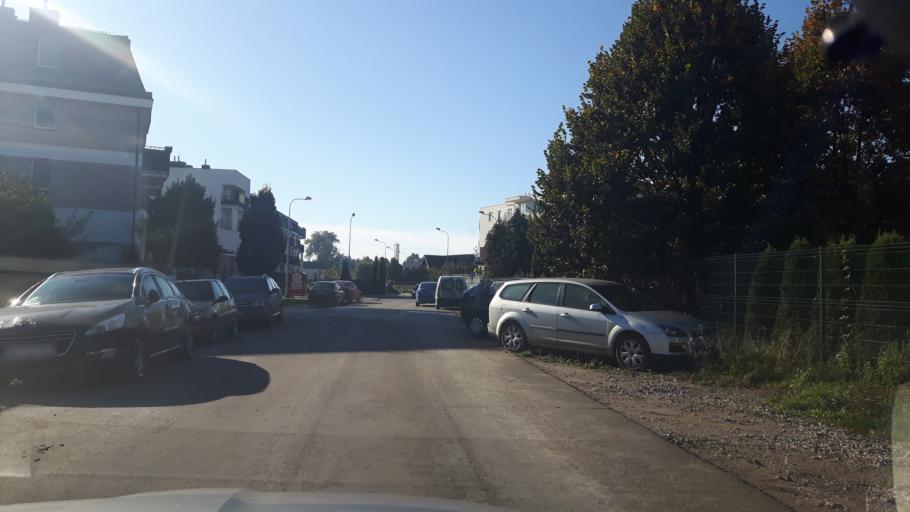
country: PL
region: Masovian Voivodeship
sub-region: Powiat legionowski
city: Stanislawow Pierwszy
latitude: 52.3617
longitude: 21.0391
